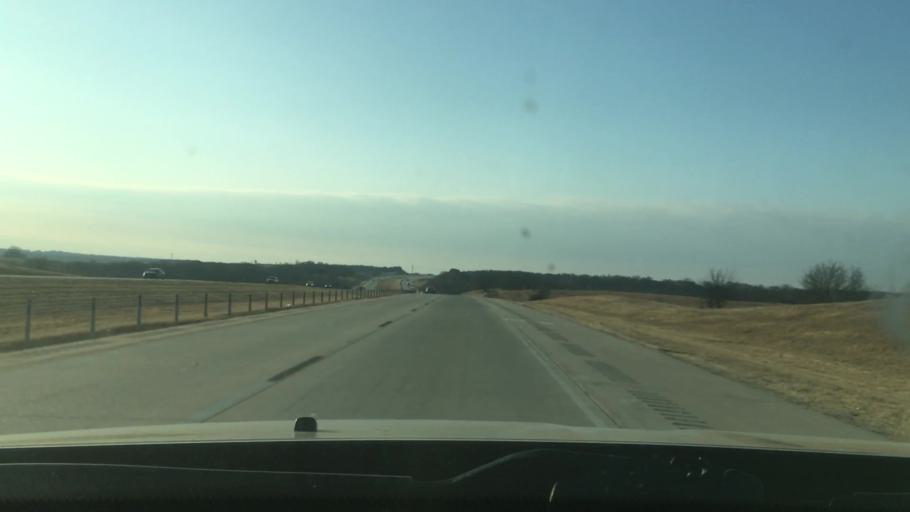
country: US
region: Oklahoma
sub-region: Carter County
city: Ardmore
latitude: 34.2523
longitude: -97.1650
